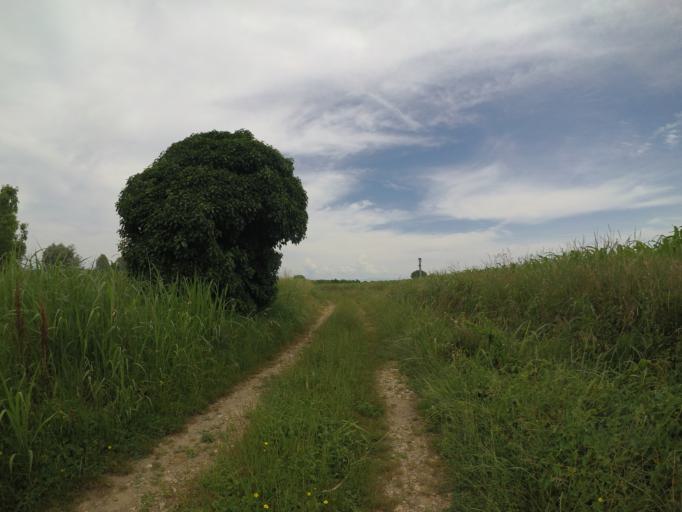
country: IT
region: Friuli Venezia Giulia
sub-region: Provincia di Udine
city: Bertiolo
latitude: 45.9358
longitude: 13.0540
